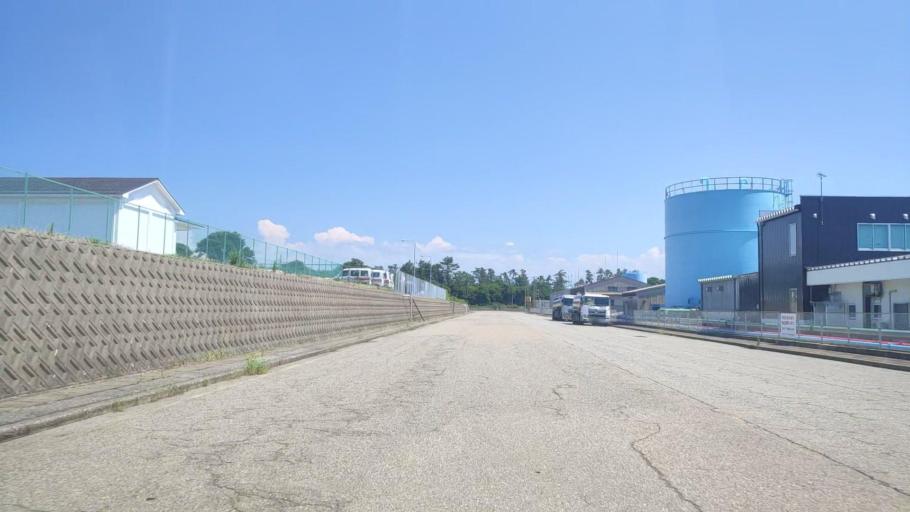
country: JP
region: Ishikawa
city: Kanazawa-shi
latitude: 36.6201
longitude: 136.6122
